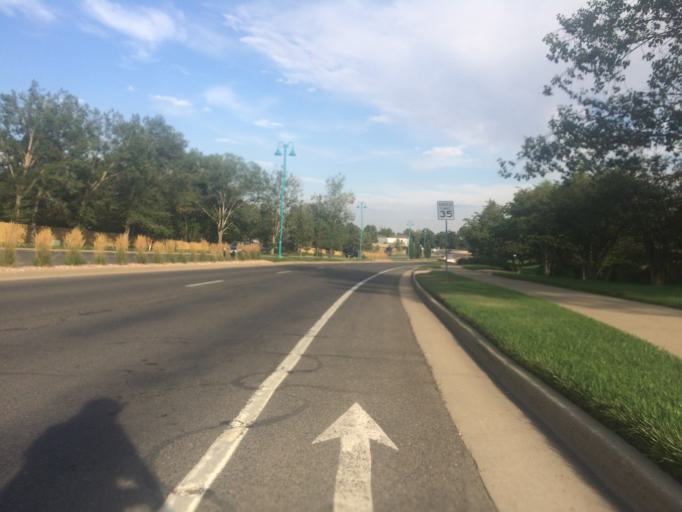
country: US
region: Colorado
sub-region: Boulder County
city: Superior
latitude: 39.9387
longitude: -105.1506
